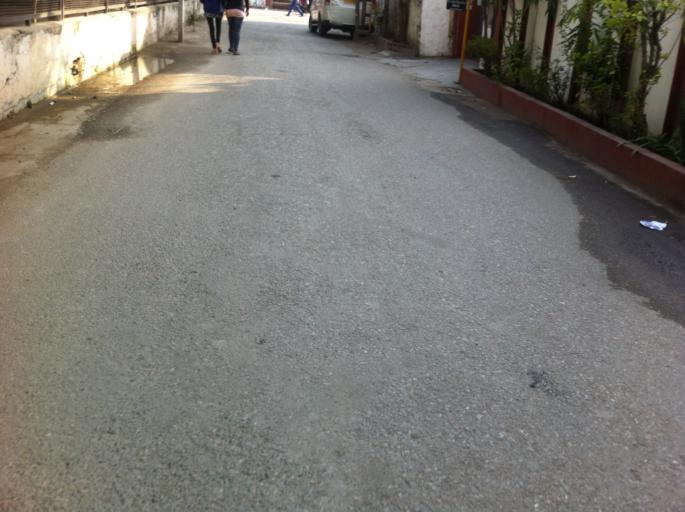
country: IN
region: Punjab
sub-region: Kapurthala
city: Phagwara
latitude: 31.2150
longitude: 75.7736
